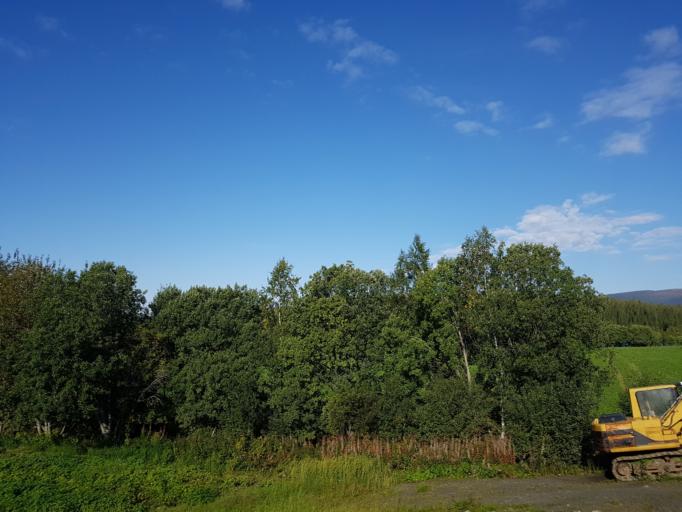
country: NO
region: Sor-Trondelag
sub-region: Trondheim
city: Trondheim
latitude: 63.6201
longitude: 10.2381
